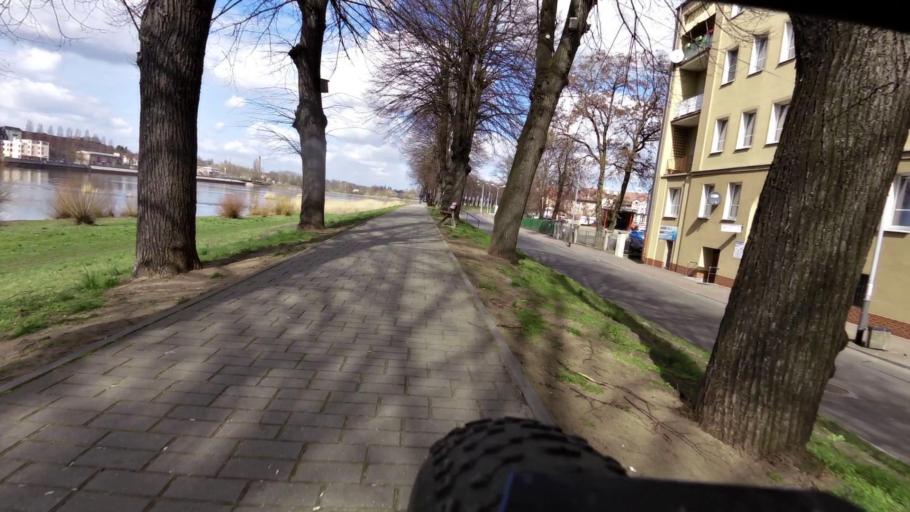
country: PL
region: Lubusz
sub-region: Powiat slubicki
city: Slubice
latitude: 52.3506
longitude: 14.5562
